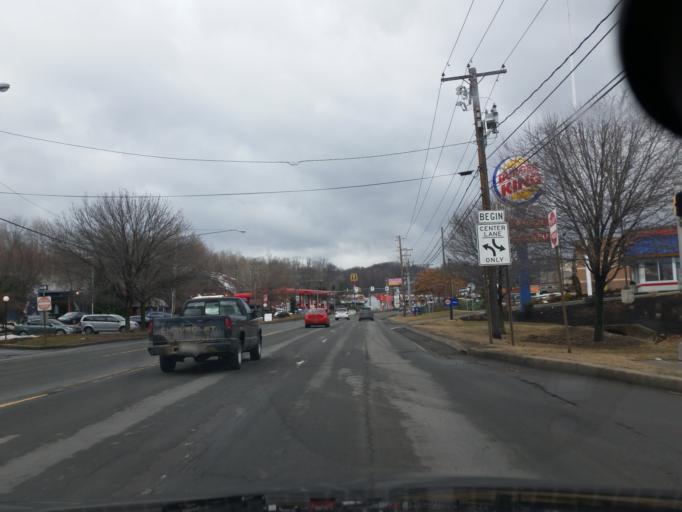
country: US
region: Pennsylvania
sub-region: Lackawanna County
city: Clarks Green
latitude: 41.4841
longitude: -75.6921
